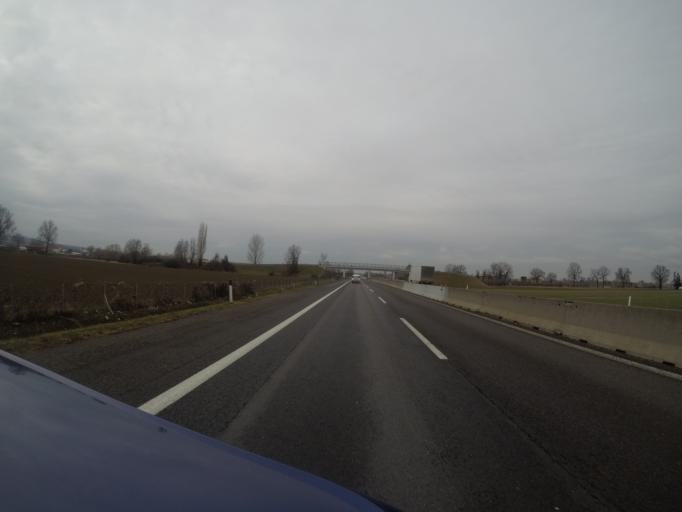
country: IT
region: Emilia-Romagna
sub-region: Provincia di Bologna
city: Ponte Ronca
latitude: 44.5058
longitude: 11.2049
